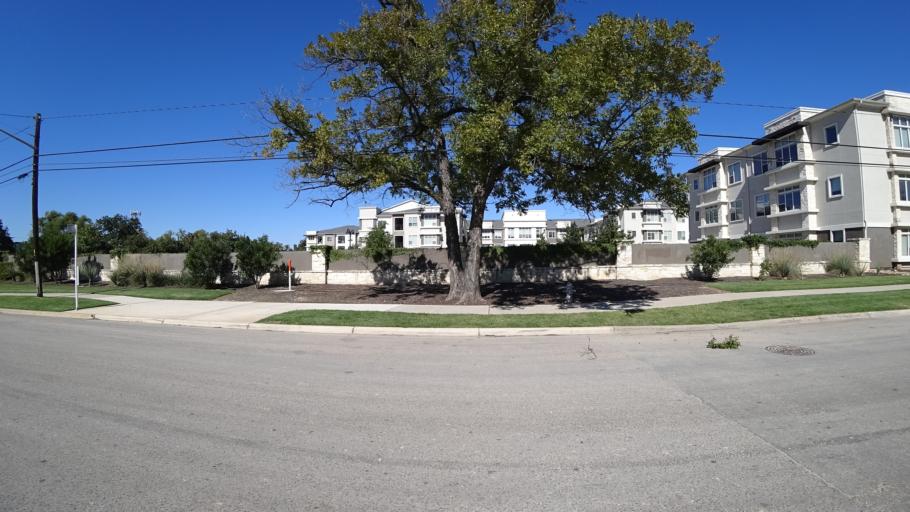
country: US
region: Texas
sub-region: Travis County
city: Austin
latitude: 30.2410
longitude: -97.7243
